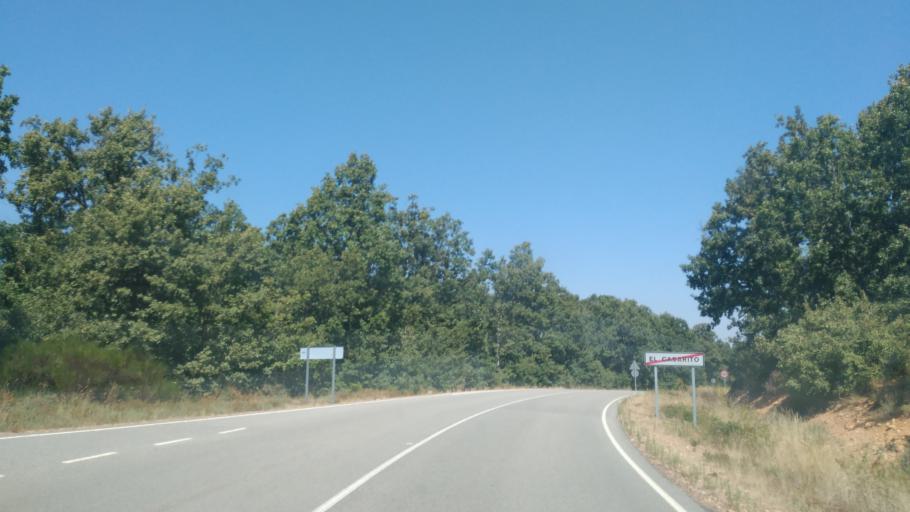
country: ES
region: Castille and Leon
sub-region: Provincia de Salamanca
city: Nava de Francia
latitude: 40.5269
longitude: -6.1384
